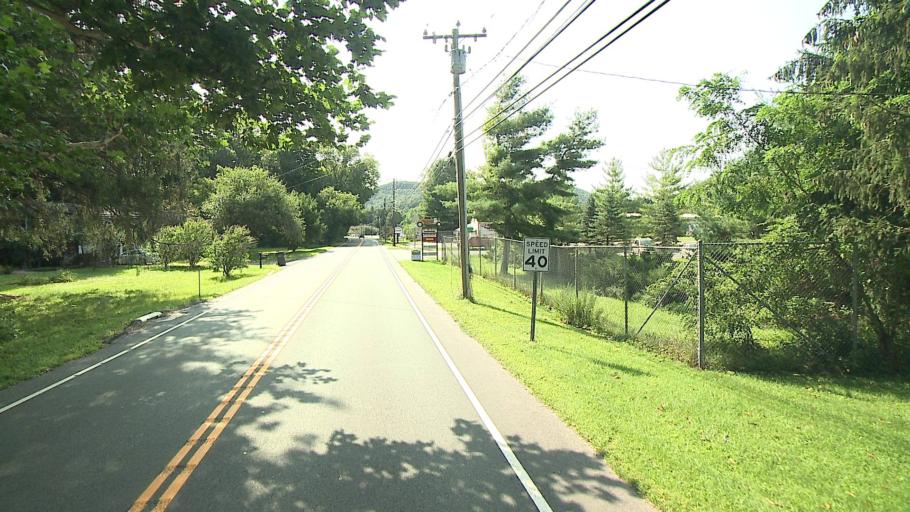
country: US
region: Connecticut
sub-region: Fairfield County
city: Sherman
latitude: 41.6411
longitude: -73.4832
